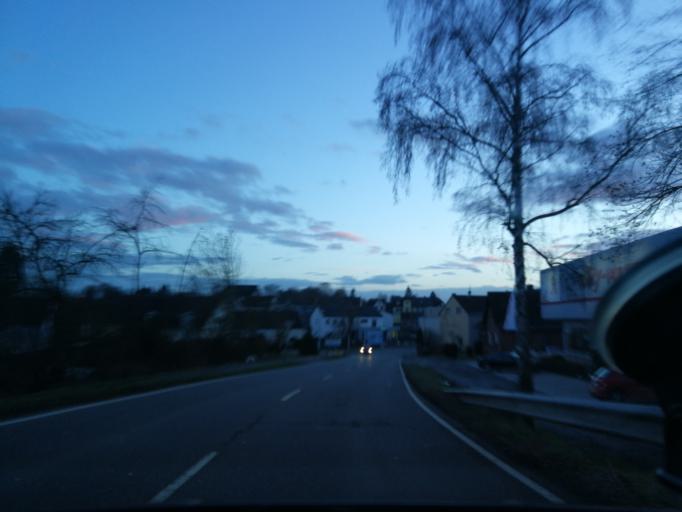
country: DE
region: Rheinland-Pfalz
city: Kenn
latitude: 49.8250
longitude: 6.7046
